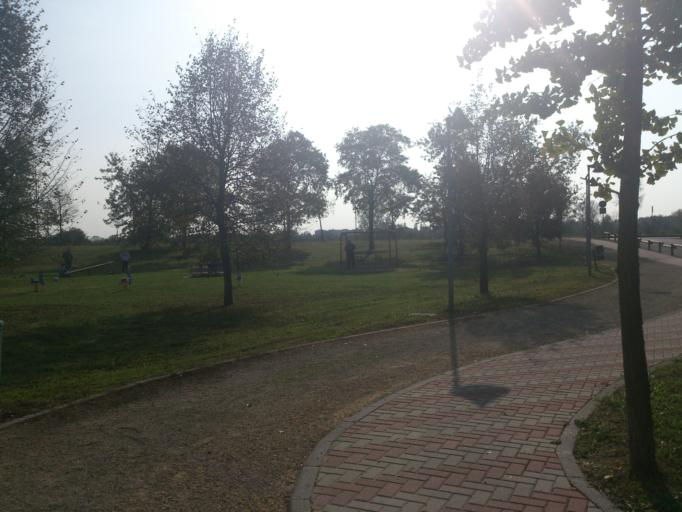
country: IT
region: Lombardy
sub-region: Citta metropolitana di Milano
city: San Donato Milanese
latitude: 45.4121
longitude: 9.2791
